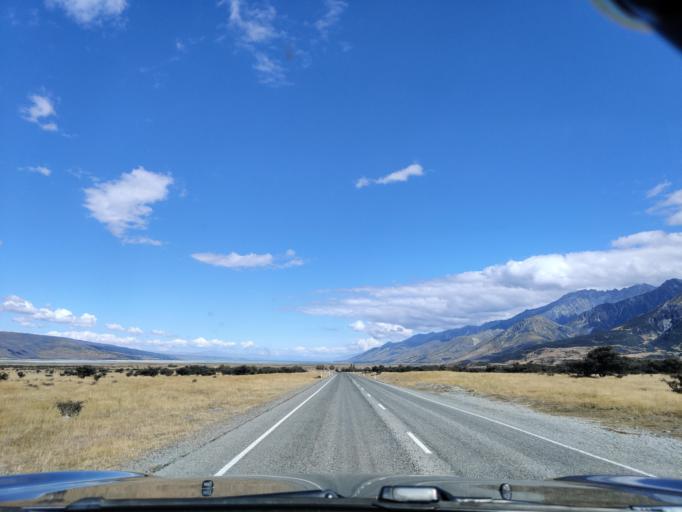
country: NZ
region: Canterbury
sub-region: Timaru District
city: Pleasant Point
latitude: -43.7772
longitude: 170.1234
